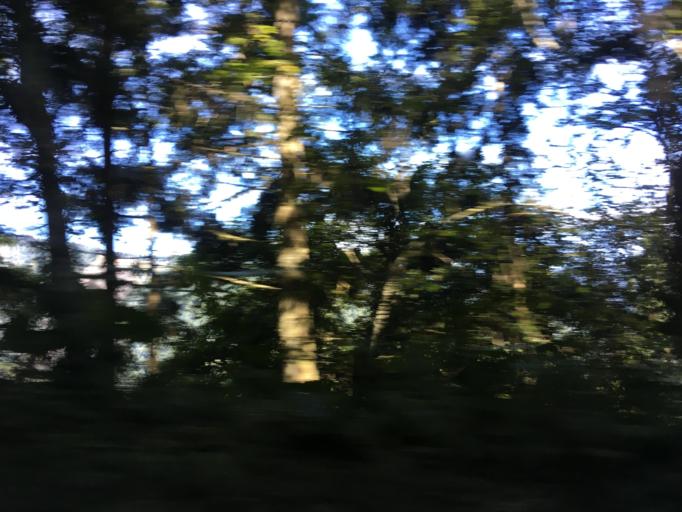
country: TW
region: Taiwan
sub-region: Yilan
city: Yilan
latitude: 24.5424
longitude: 121.5119
